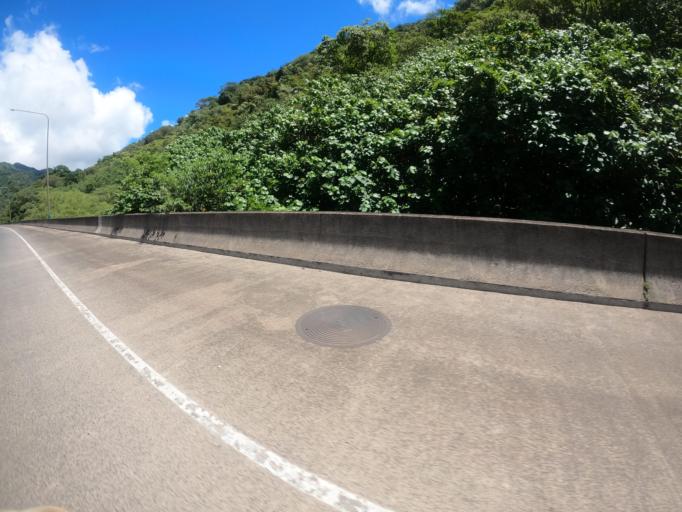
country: US
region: Hawaii
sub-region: Honolulu County
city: Halawa Heights
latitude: 21.3992
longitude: -157.8774
